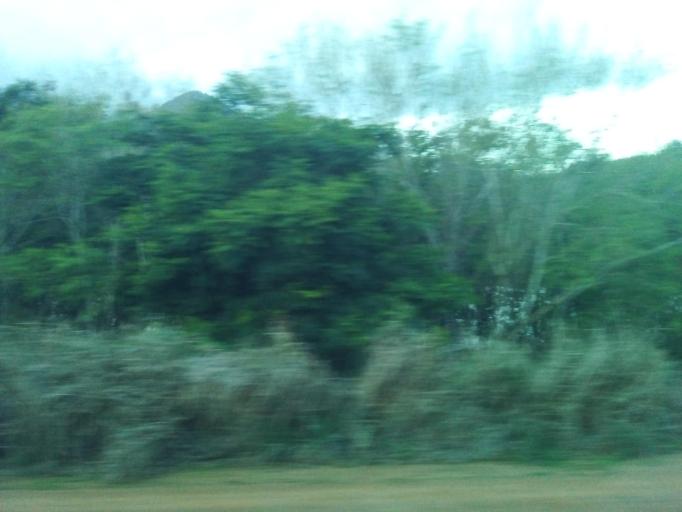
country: BR
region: Espirito Santo
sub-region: Baixo Guandu
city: Baixo Guandu
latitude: -19.5244
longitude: -40.8289
